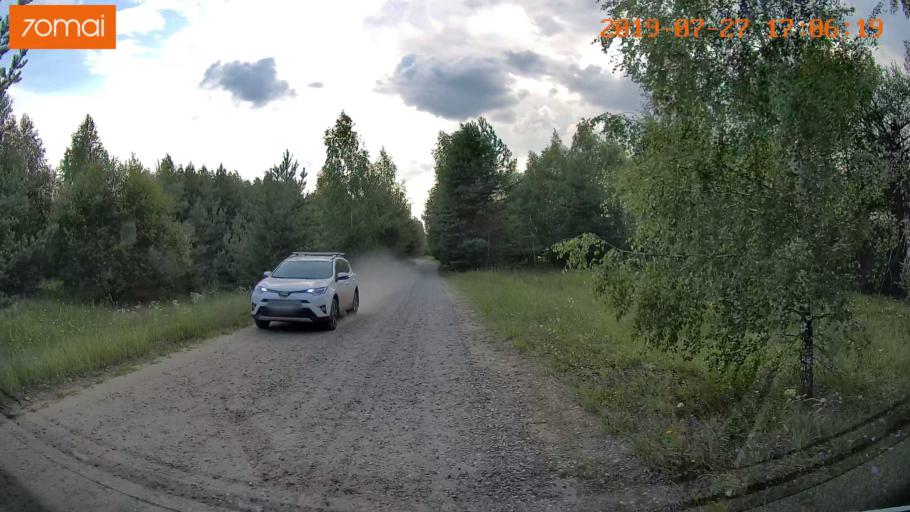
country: RU
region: Ivanovo
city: Novo-Talitsy
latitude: 57.0869
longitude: 40.8430
